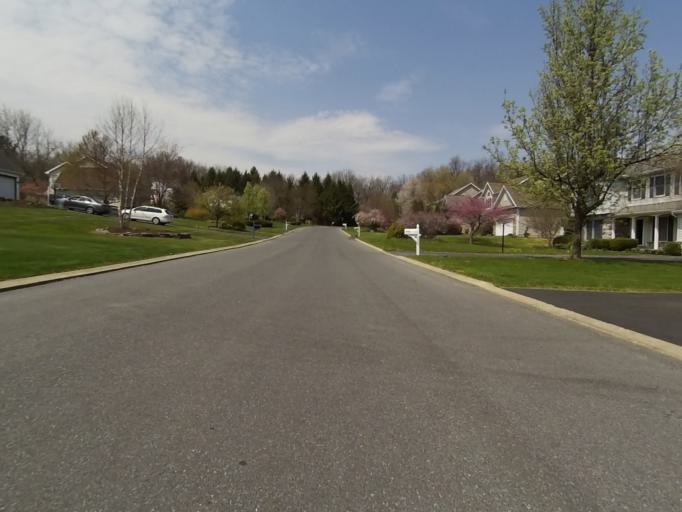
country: US
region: Pennsylvania
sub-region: Centre County
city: Park Forest Village
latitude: 40.7946
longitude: -77.9036
